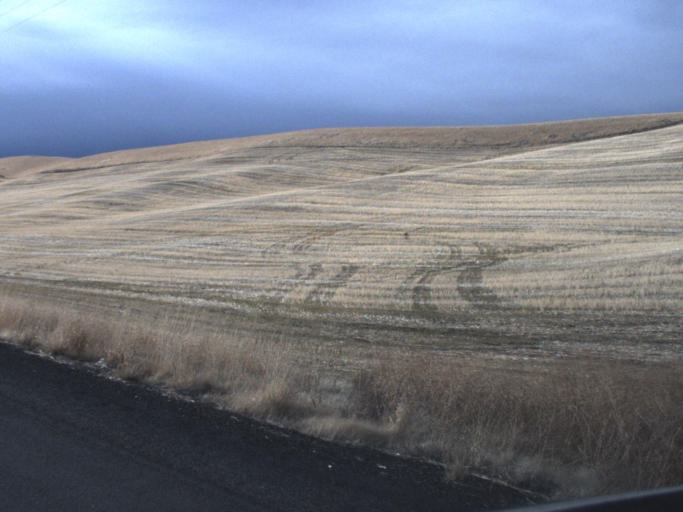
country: US
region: Washington
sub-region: Whitman County
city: Colfax
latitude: 46.8720
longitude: -117.4086
